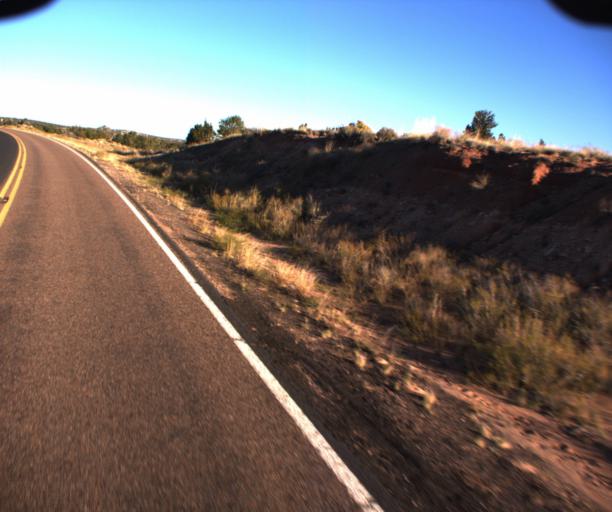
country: US
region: Arizona
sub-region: Apache County
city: Ganado
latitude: 35.4600
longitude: -109.5230
